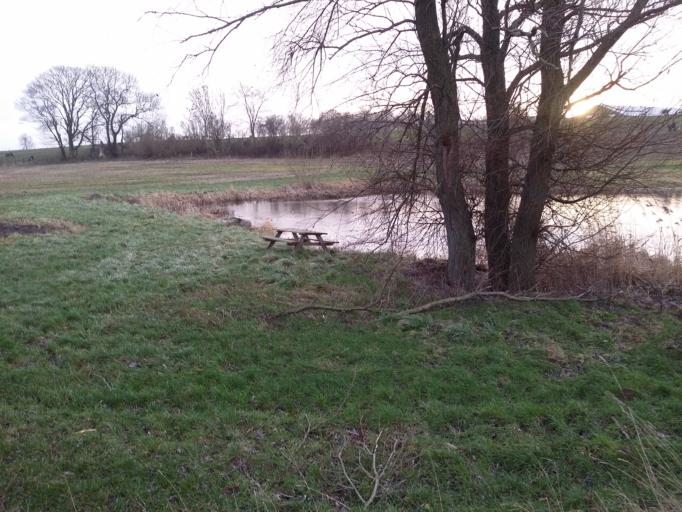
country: DK
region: Zealand
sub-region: Roskilde Kommune
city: Jyllinge
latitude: 55.7960
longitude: 12.1106
